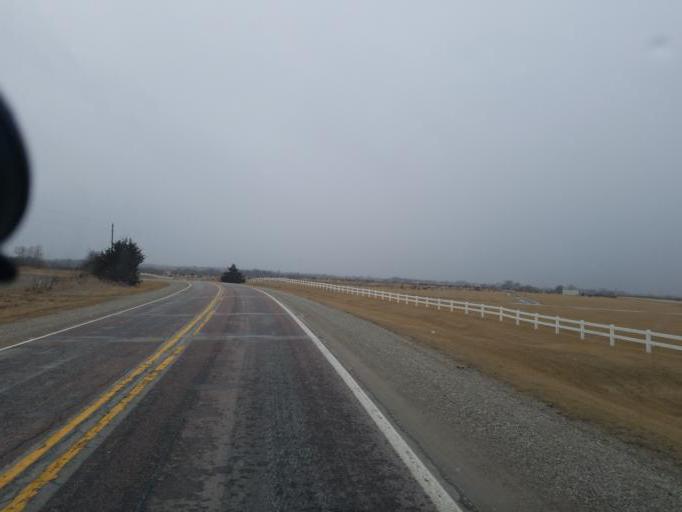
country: US
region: Iowa
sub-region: Appanoose County
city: Centerville
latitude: 40.6305
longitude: -92.9409
